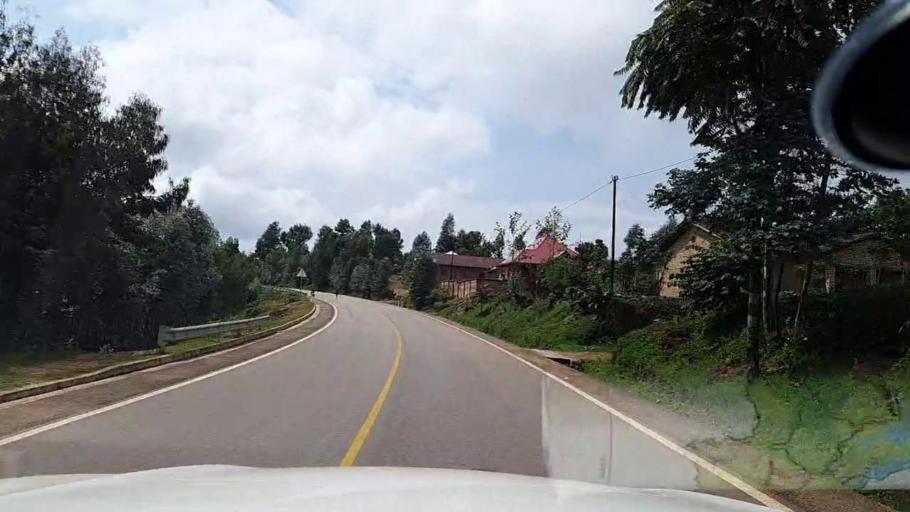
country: RW
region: Southern Province
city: Nzega
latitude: -2.4960
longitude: 29.5065
